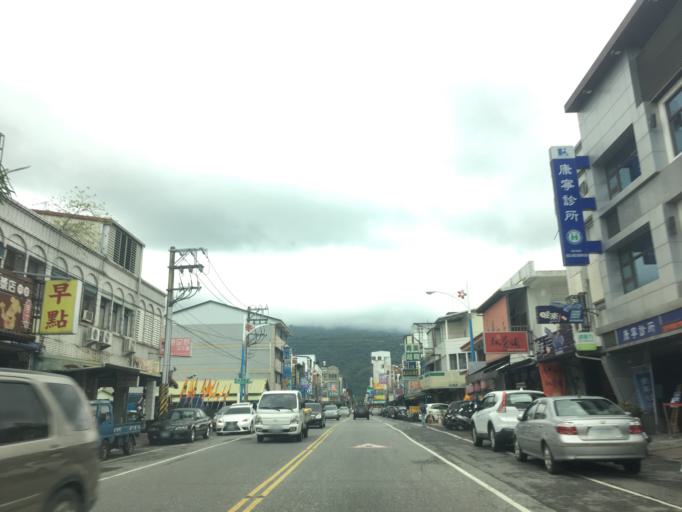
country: TW
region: Taiwan
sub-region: Hualien
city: Hualian
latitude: 23.9788
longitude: 121.5689
